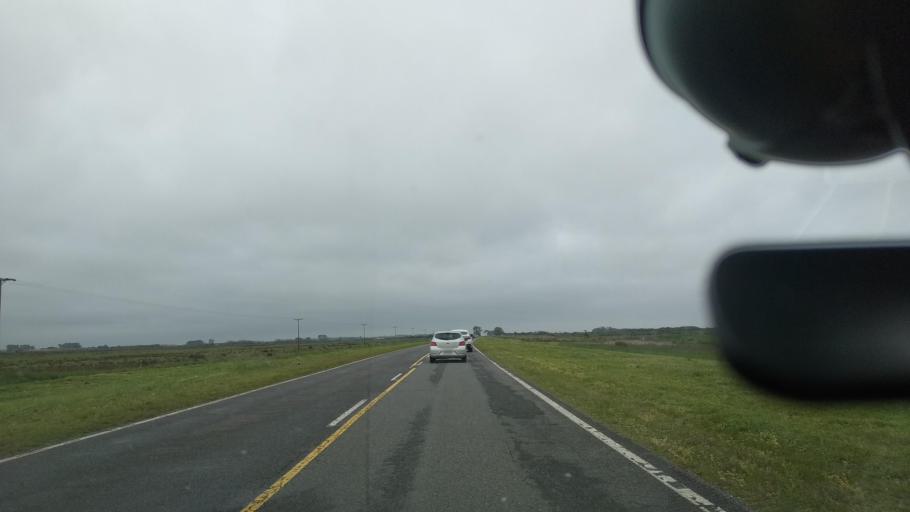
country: AR
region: Buenos Aires
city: Veronica
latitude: -35.6036
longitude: -57.2787
